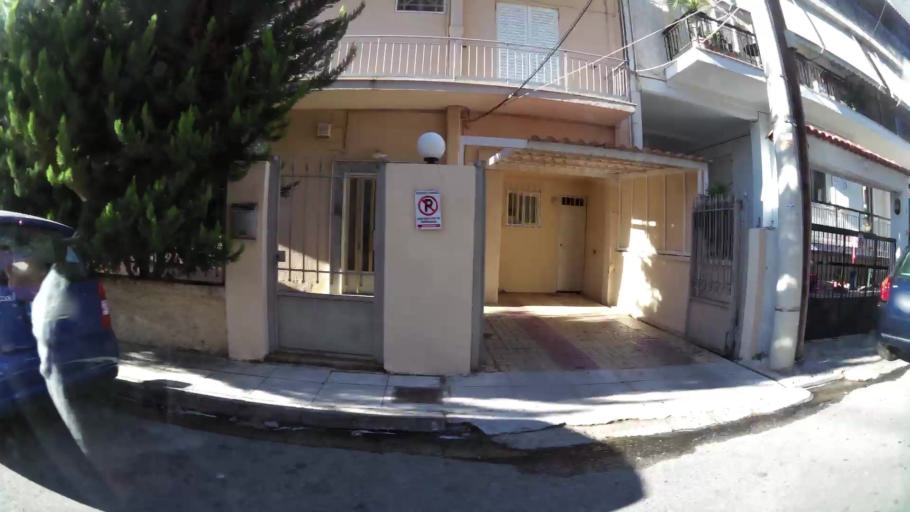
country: GR
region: Attica
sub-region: Nomarchia Anatolikis Attikis
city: Gerakas
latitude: 38.0088
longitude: 23.8570
